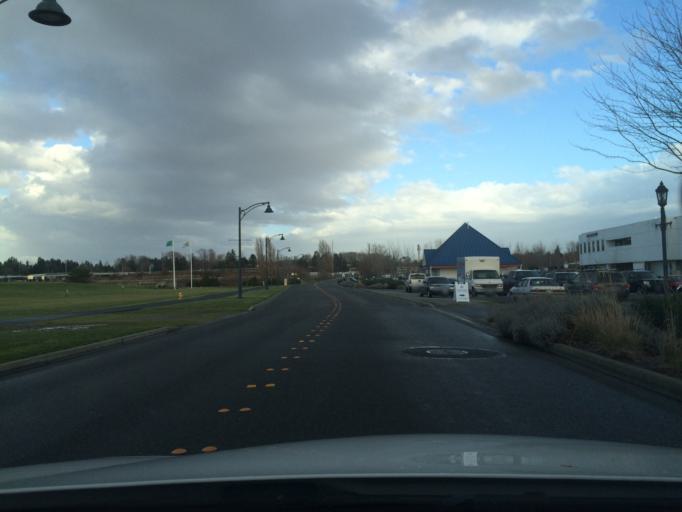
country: US
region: Washington
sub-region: Whatcom County
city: Blaine
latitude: 48.9951
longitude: -122.7586
